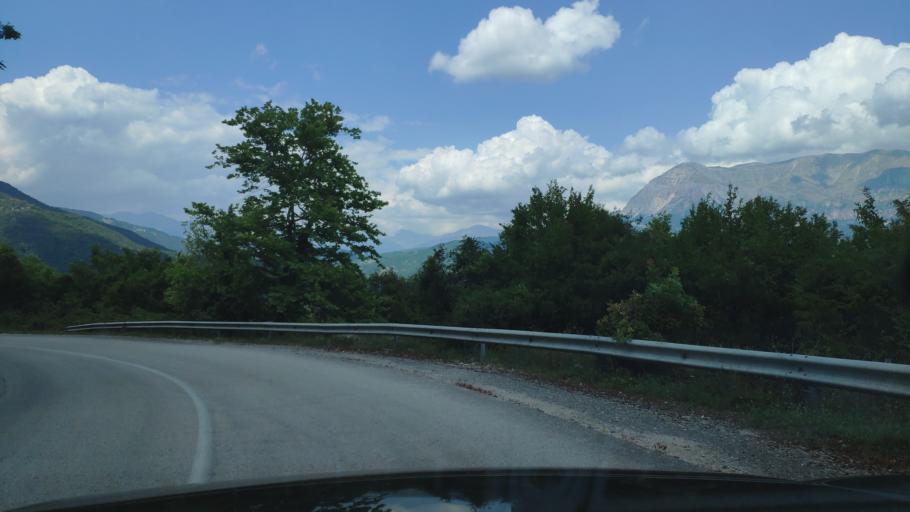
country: GR
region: Epirus
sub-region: Nomos Artas
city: Agios Dimitrios
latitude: 39.4546
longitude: 21.0235
